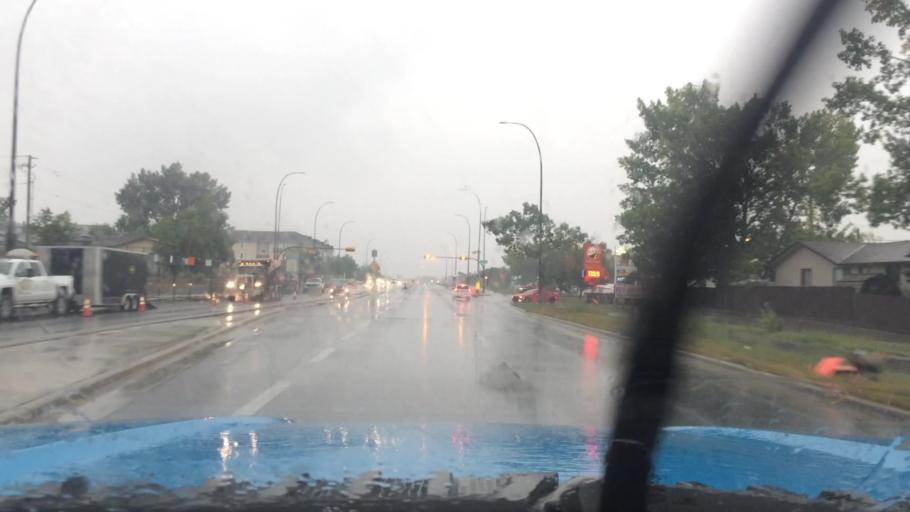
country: CA
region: Alberta
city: Calgary
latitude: 51.0902
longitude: -113.9584
